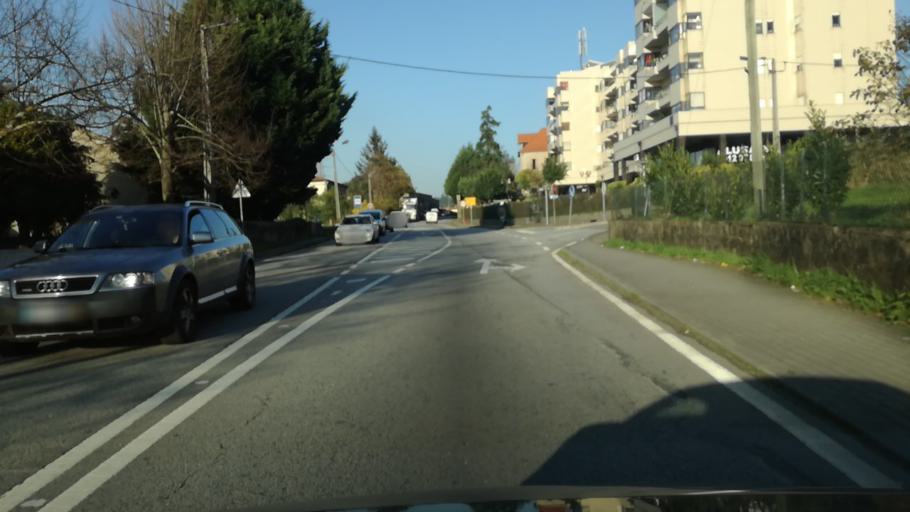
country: PT
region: Braga
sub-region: Vila Nova de Famalicao
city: Ferreiros
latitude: 41.3544
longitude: -8.5531
